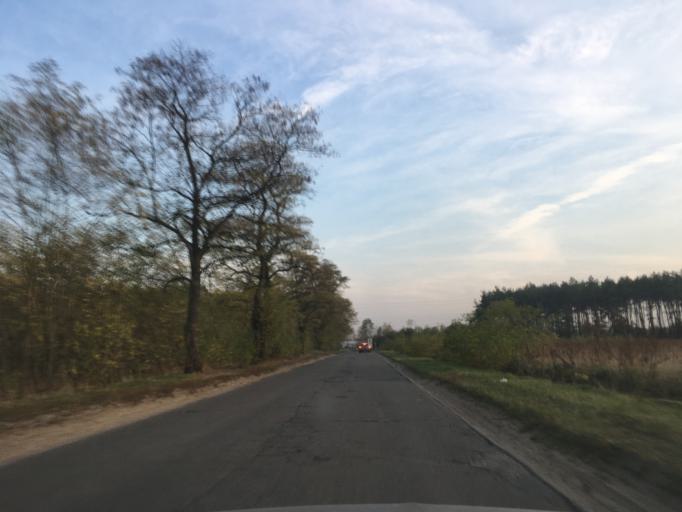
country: PL
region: Masovian Voivodeship
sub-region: Powiat piaseczynski
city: Lesznowola
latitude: 52.0645
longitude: 20.8984
